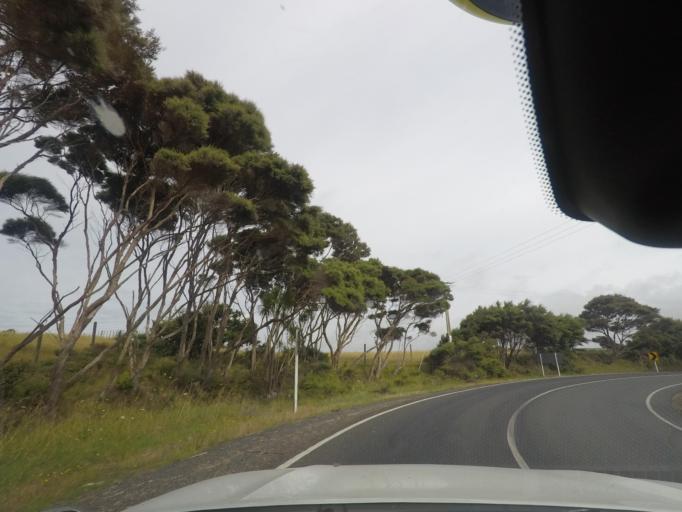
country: NZ
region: Auckland
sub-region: Auckland
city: Parakai
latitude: -36.4939
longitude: 174.2467
